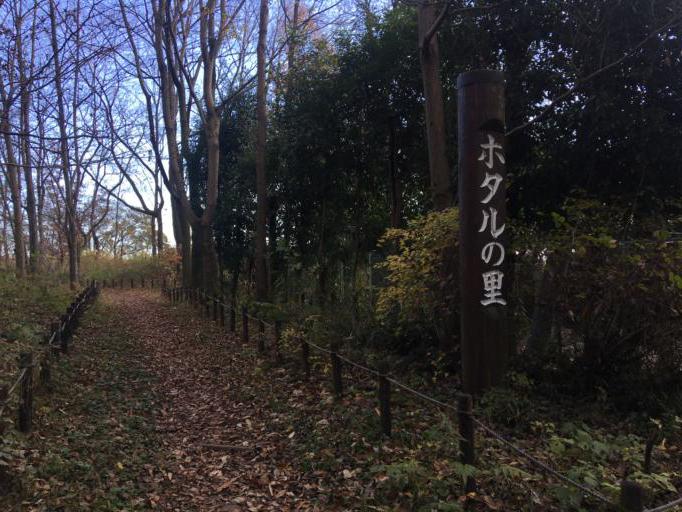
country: JP
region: Saitama
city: Ogawa
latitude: 36.0342
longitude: 139.3213
